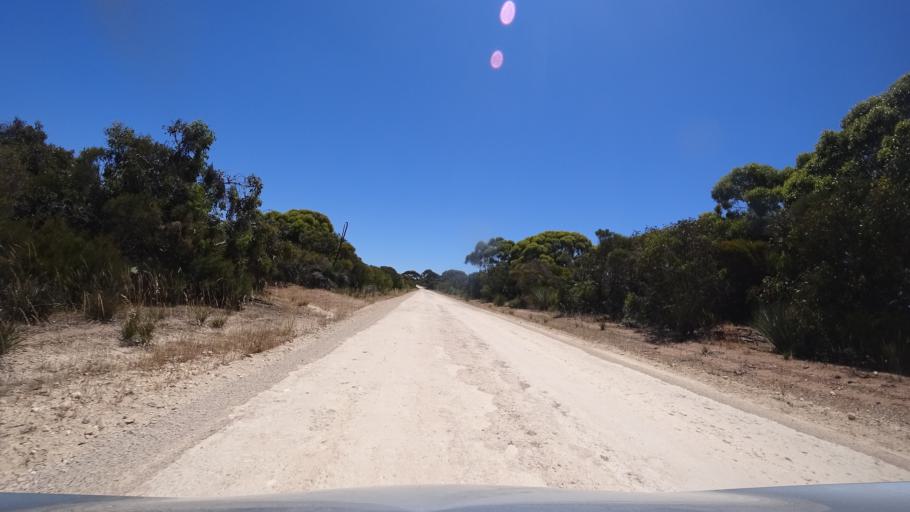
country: AU
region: South Australia
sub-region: Kangaroo Island
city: Kingscote
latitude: -35.6680
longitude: 137.1061
